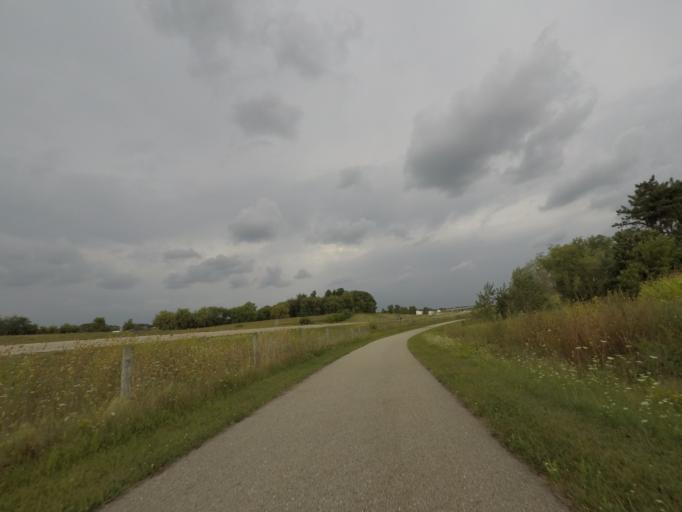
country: US
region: Wisconsin
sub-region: Jefferson County
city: Jefferson
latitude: 42.9788
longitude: -88.8234
